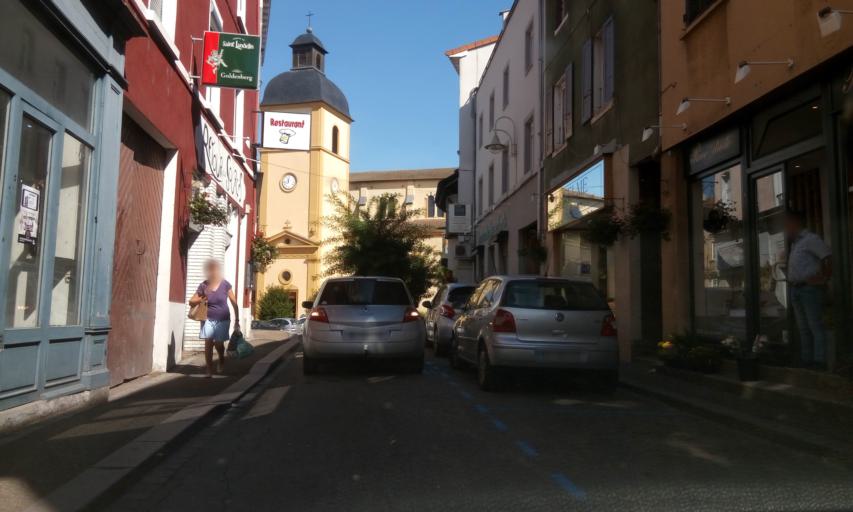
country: FR
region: Rhone-Alpes
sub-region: Departement du Rhone
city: Amplepuis
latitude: 45.9723
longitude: 4.3328
